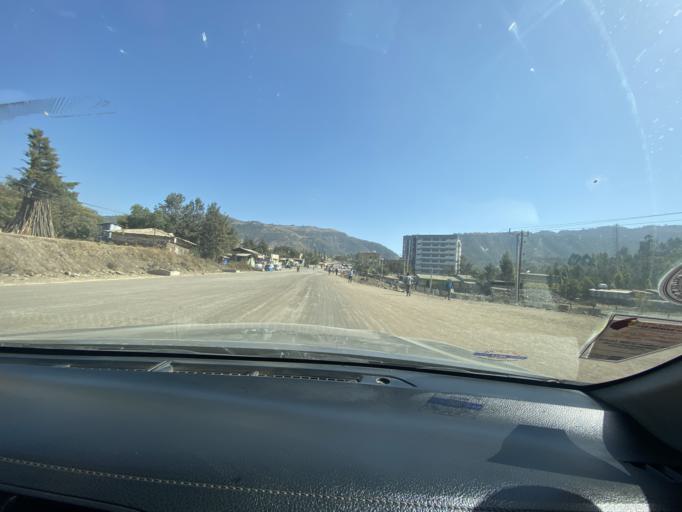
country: ET
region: Amhara
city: Robit
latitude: 11.8251
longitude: 39.5918
